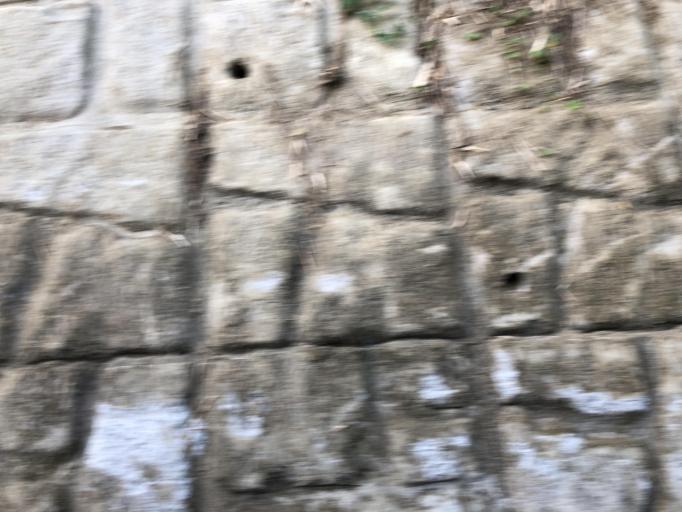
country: TW
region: Taiwan
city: Yujing
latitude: 23.0181
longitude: 120.3825
